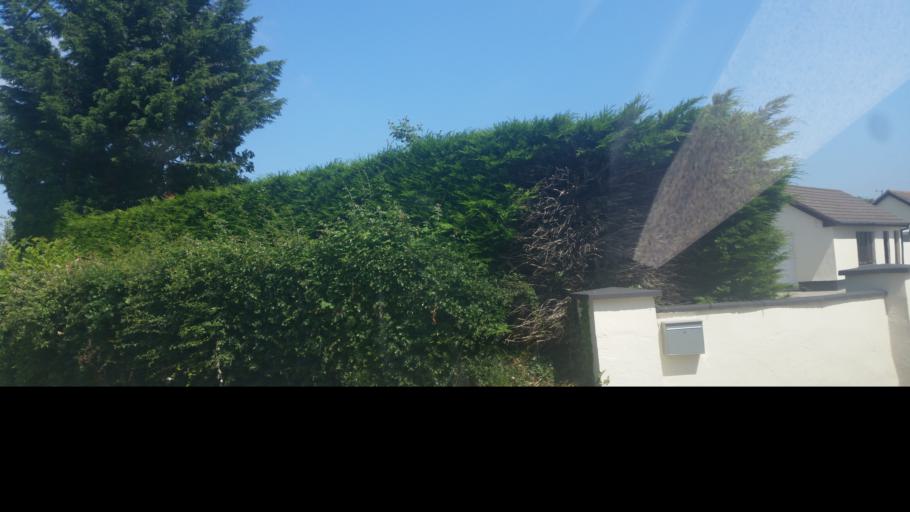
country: IE
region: Leinster
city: Lusk
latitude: 53.5313
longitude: -6.2364
